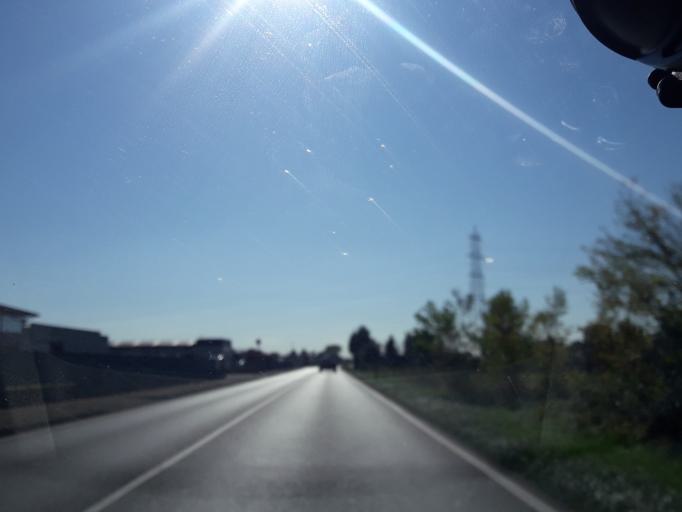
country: IT
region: Friuli Venezia Giulia
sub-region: Provincia di Udine
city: Povoletto
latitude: 46.0933
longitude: 13.2909
